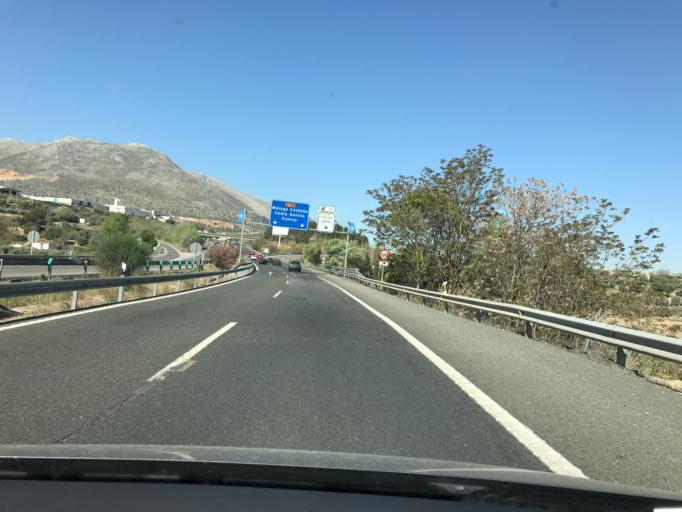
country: ES
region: Andalusia
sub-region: Provincia de Granada
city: Loja
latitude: 37.1633
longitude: -4.1178
